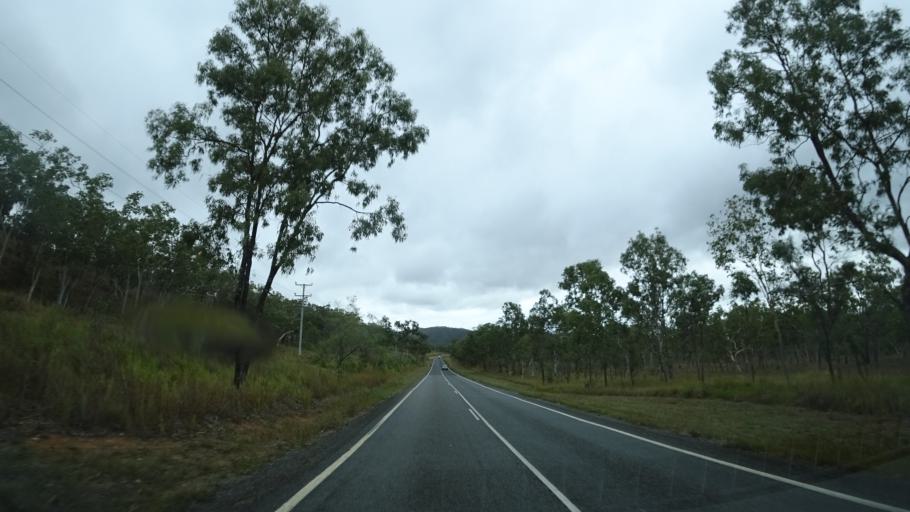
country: AU
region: Queensland
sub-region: Cairns
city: Port Douglas
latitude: -16.7107
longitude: 145.3504
